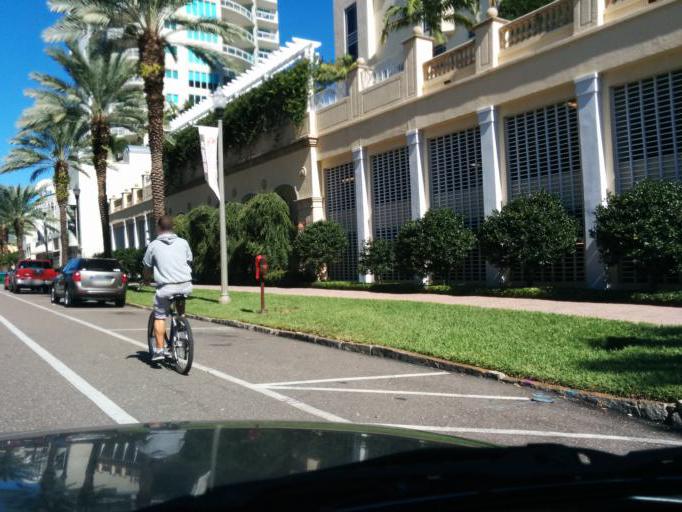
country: US
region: Florida
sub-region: Pinellas County
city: Saint Petersburg
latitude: 27.7722
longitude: -82.6339
